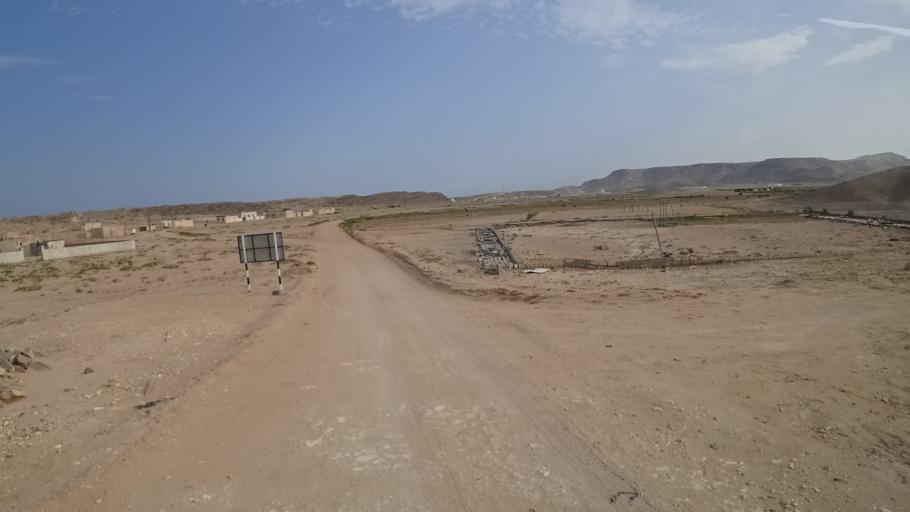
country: OM
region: Ash Sharqiyah
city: Sur
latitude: 22.4510
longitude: 59.8253
